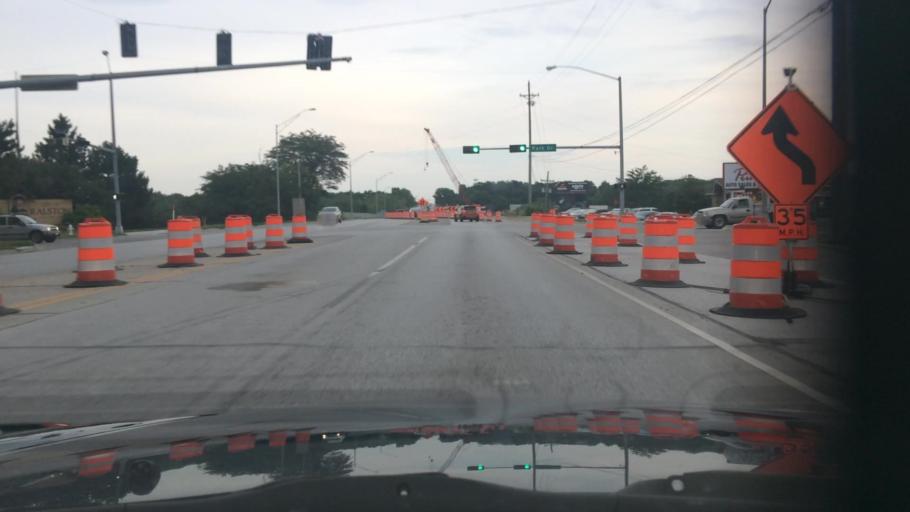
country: US
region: Nebraska
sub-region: Douglas County
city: Ralston
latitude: 41.2011
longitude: -96.0431
